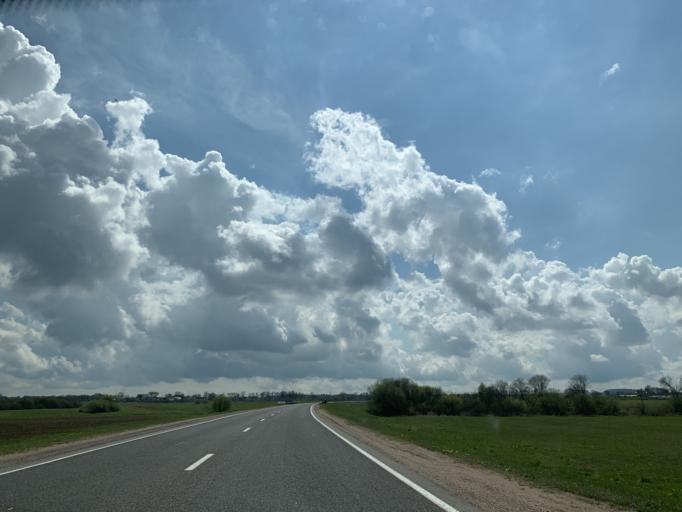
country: BY
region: Minsk
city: Nyasvizh
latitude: 53.2361
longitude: 26.7171
